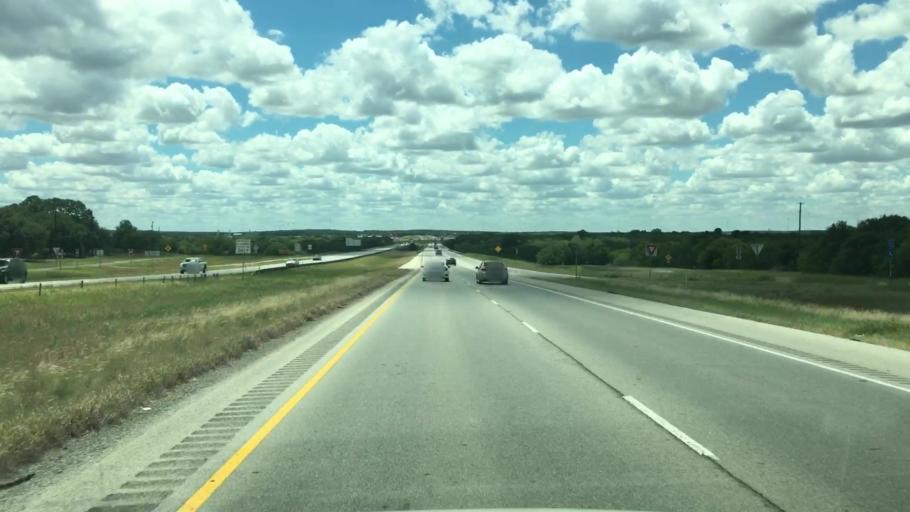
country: US
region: Texas
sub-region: Bexar County
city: Elmendorf
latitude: 29.2396
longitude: -98.4006
